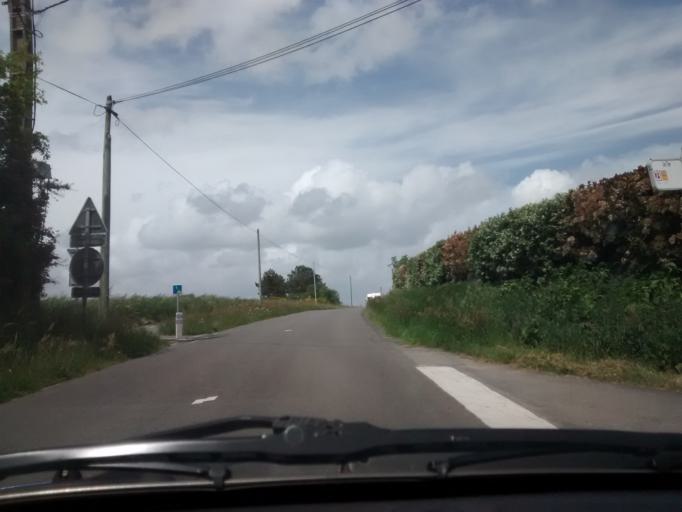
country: FR
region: Brittany
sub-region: Departement du Morbihan
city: Larmor-Baden
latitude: 47.6052
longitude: -2.8903
